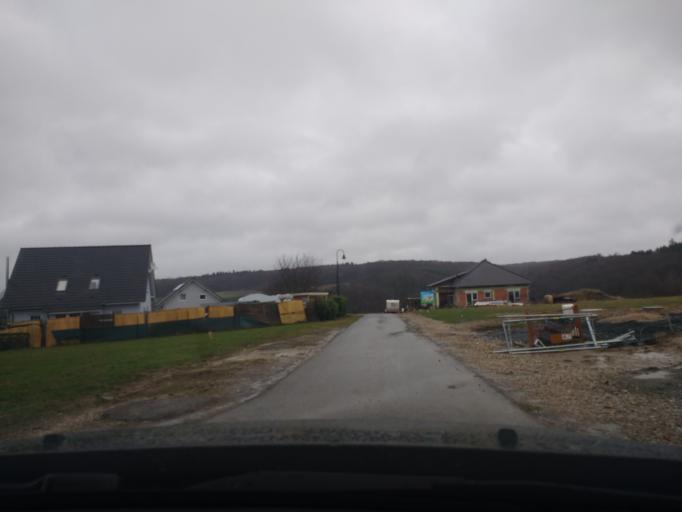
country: DE
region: Rheinland-Pfalz
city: Lotzbeuren
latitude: 49.9357
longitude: 7.2260
